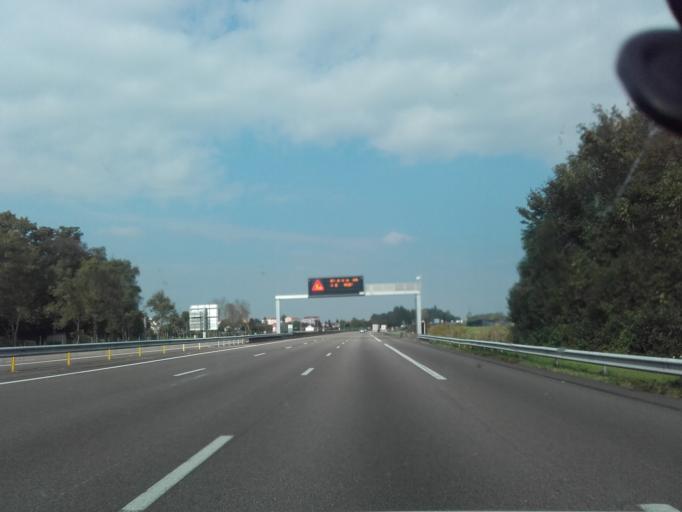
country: FR
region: Bourgogne
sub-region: Departement de Saone-et-Loire
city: Chatenoy-le-Royal
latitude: 46.7849
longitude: 4.8199
